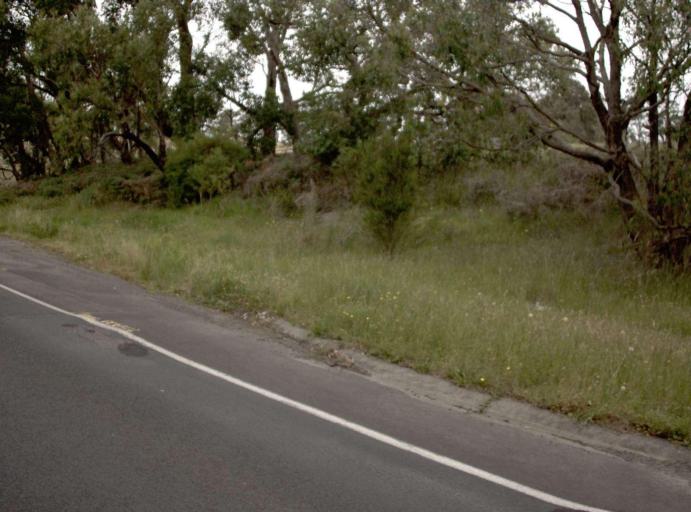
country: AU
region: Victoria
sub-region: Cardinia
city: Koo-Wee-Rup
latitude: -38.3404
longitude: 145.6294
